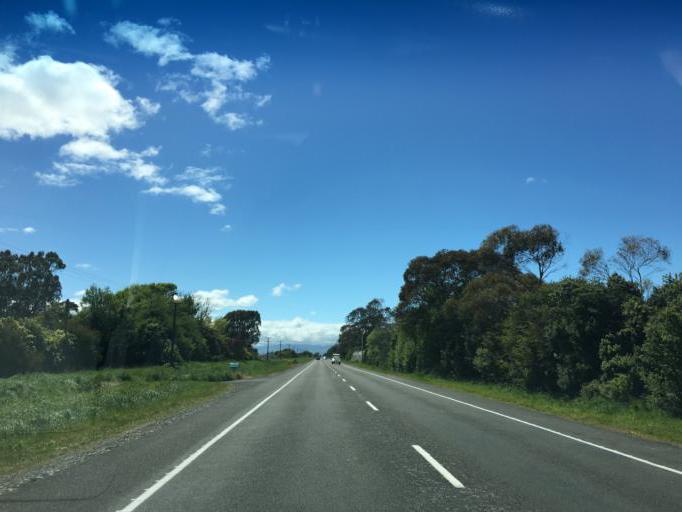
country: NZ
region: Manawatu-Wanganui
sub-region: Palmerston North City
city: Palmerston North
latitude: -40.3965
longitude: 175.5143
